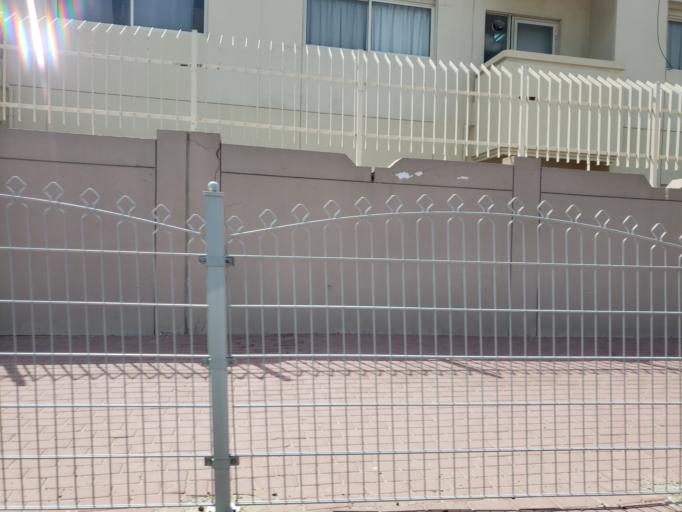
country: AE
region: Dubai
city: Dubai
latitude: 25.1074
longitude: 55.1703
